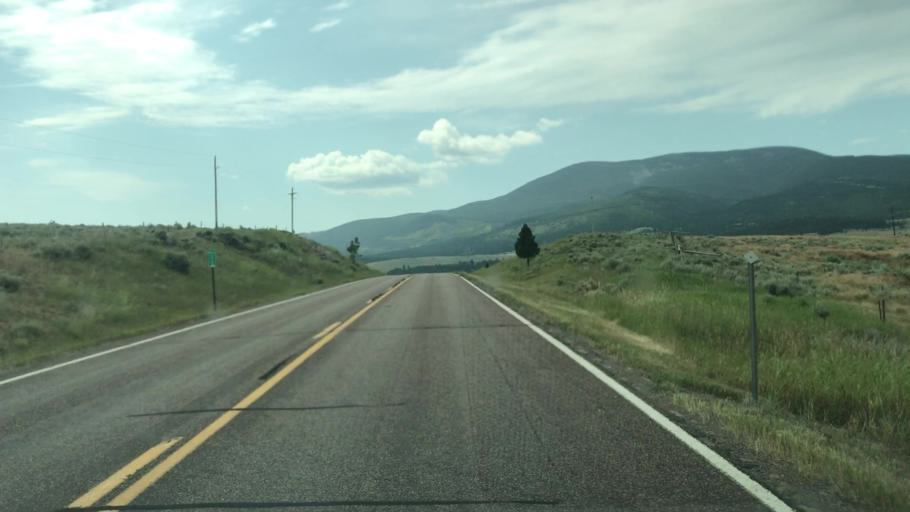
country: US
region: Montana
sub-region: Lewis and Clark County
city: Lincoln
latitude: 46.8458
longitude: -112.9018
